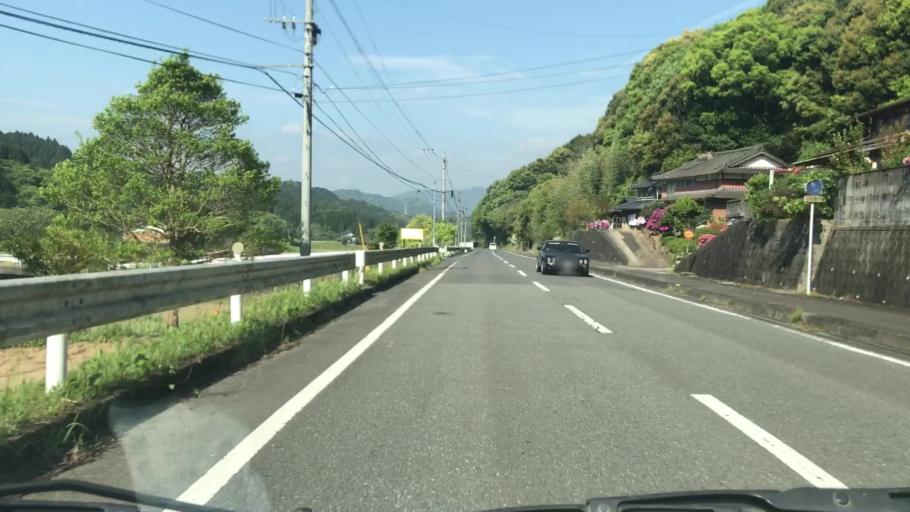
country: JP
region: Saga Prefecture
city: Takeocho-takeo
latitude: 33.2152
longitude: 129.9948
